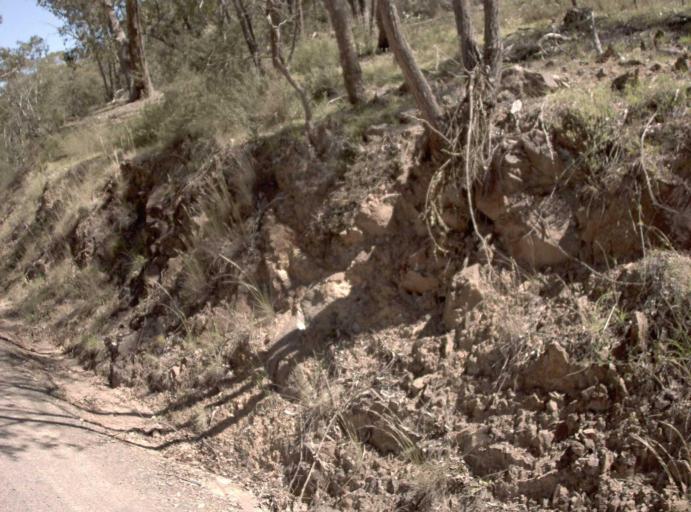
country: AU
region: New South Wales
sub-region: Bombala
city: Bombala
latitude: -37.1189
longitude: 148.6594
